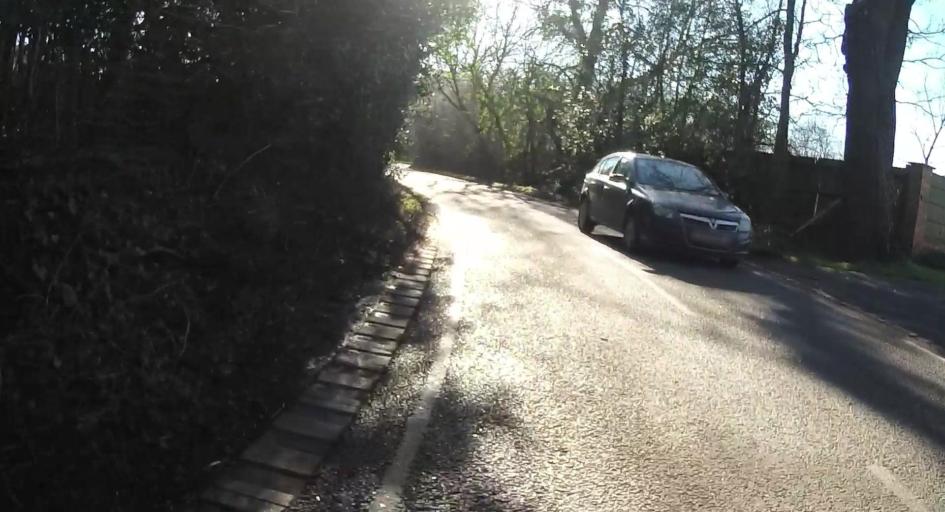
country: GB
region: England
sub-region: Surrey
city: Chobham
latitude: 51.3504
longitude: -0.5801
